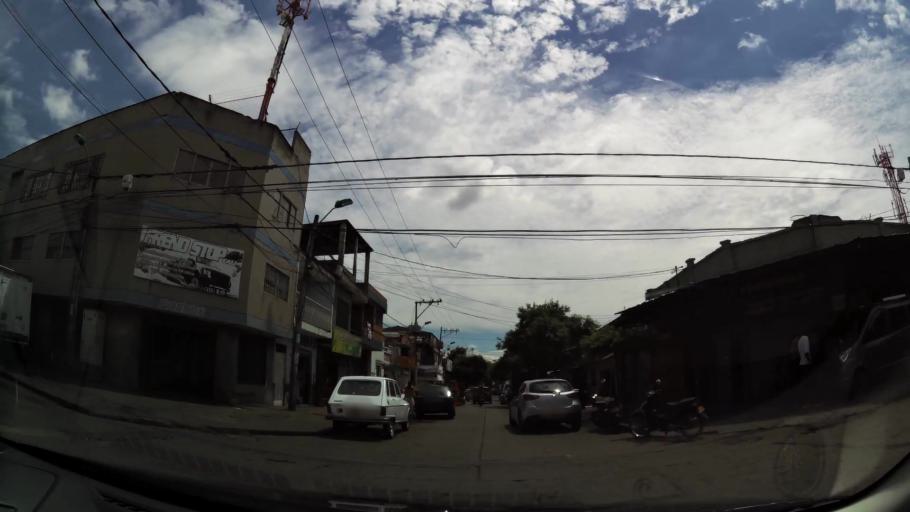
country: CO
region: Valle del Cauca
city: Cali
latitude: 3.4456
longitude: -76.5202
